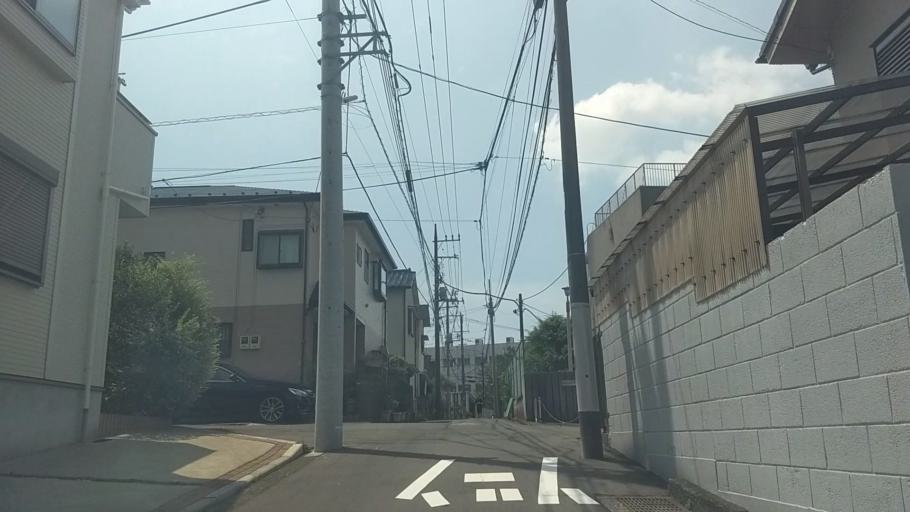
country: JP
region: Kanagawa
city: Yokohama
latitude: 35.4994
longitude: 139.6600
